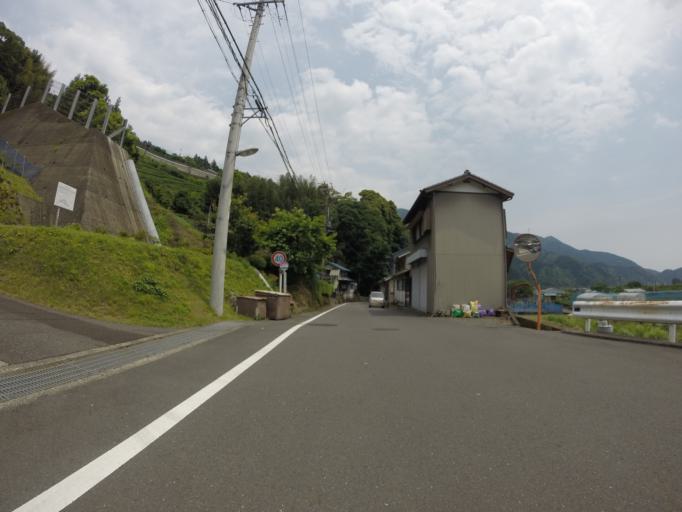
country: JP
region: Shizuoka
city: Shizuoka-shi
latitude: 35.1015
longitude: 138.3694
